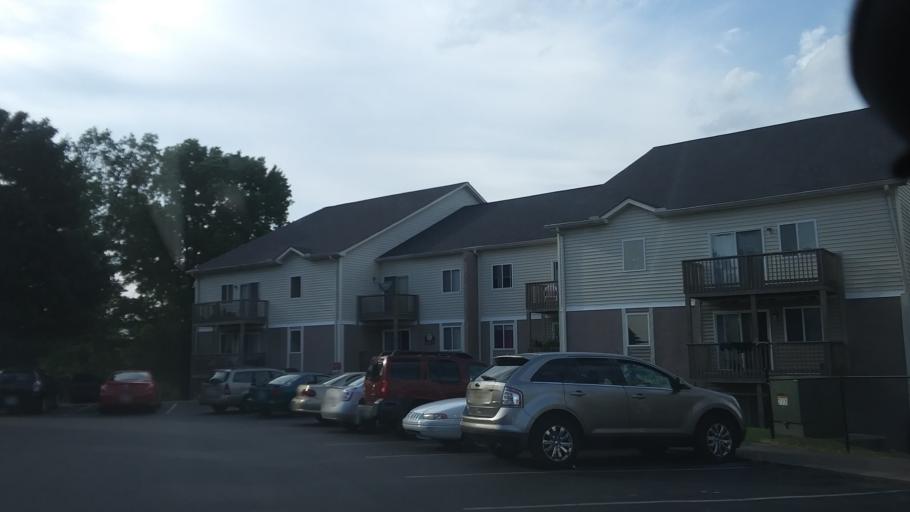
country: US
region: Tennessee
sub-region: Davidson County
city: Oak Hill
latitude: 36.0838
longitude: -86.7150
